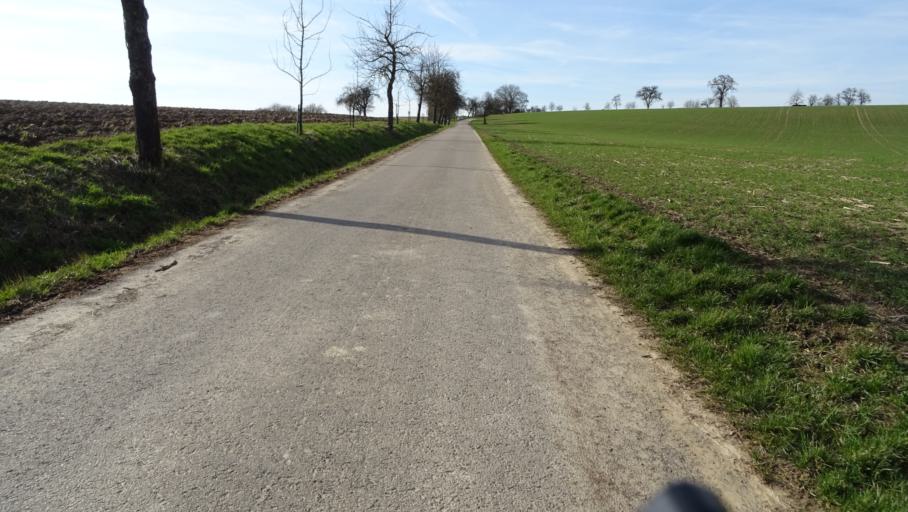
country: DE
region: Baden-Wuerttemberg
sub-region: Karlsruhe Region
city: Seckach
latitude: 49.4129
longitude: 9.2974
